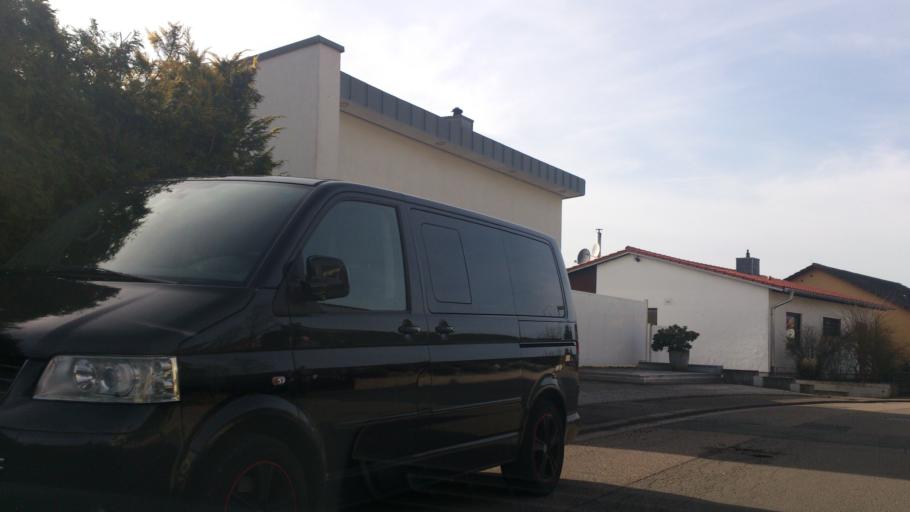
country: DE
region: Rheinland-Pfalz
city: Zweibrucken
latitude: 49.2692
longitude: 7.3236
